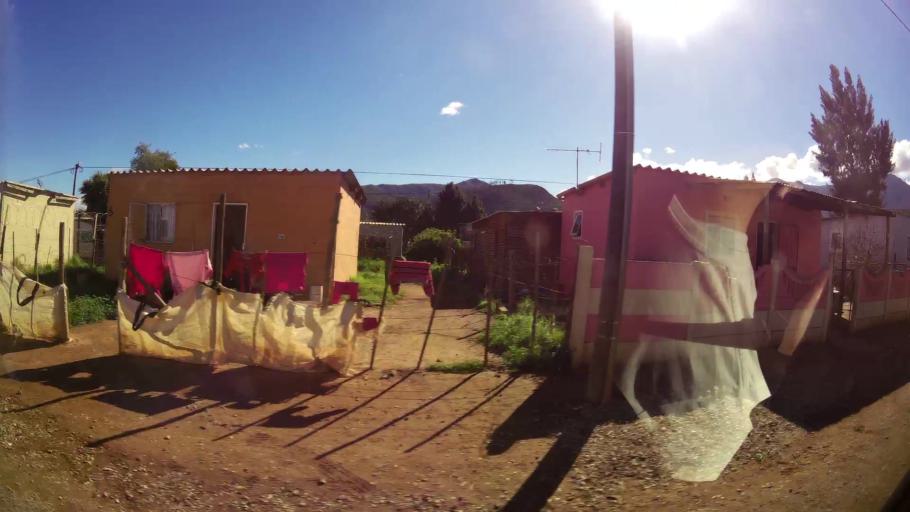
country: ZA
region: Western Cape
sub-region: Cape Winelands District Municipality
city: Ashton
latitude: -33.7923
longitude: 19.8803
